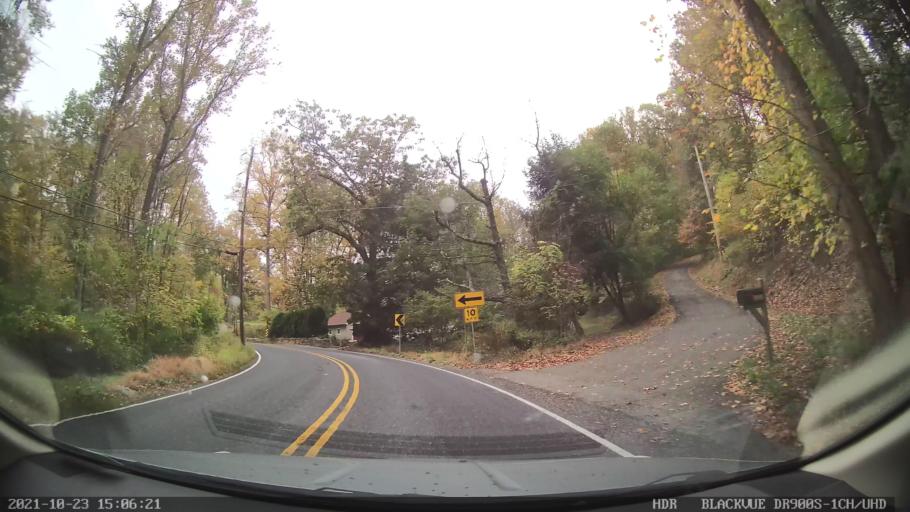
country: US
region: Pennsylvania
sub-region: Berks County
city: Bally
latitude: 40.4356
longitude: -75.5916
